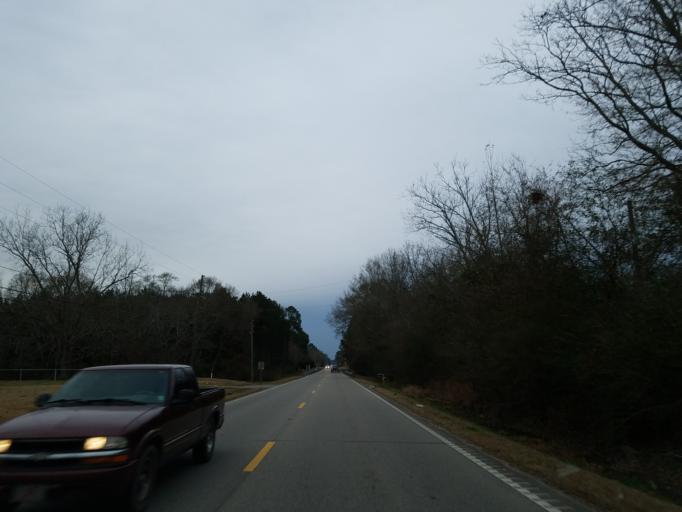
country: US
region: Mississippi
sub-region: Forrest County
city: Glendale
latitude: 31.4916
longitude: -89.2810
